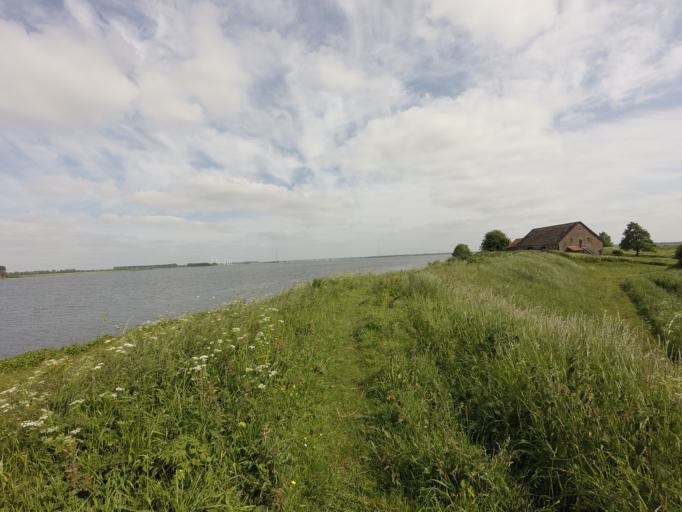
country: NL
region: North Brabant
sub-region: Gemeente Moerdijk
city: Willemstad
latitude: 51.7348
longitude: 4.3567
